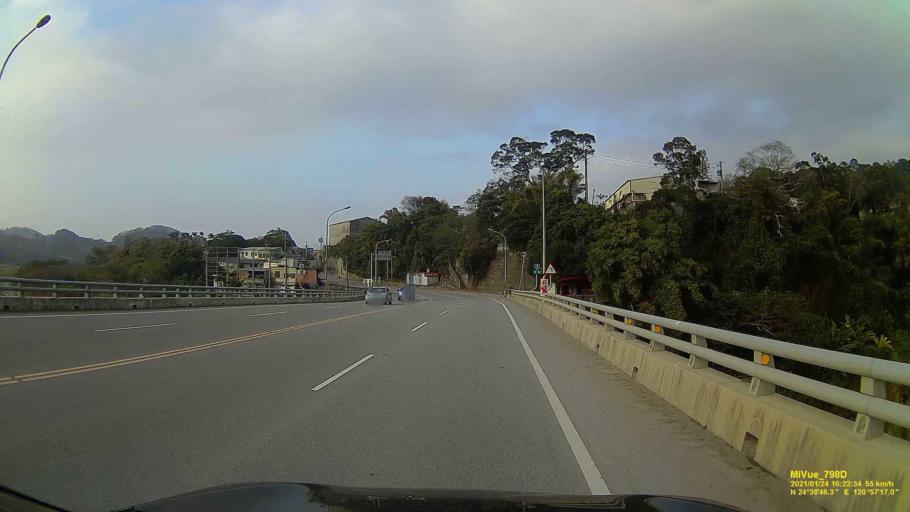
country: TW
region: Taiwan
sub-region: Miaoli
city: Miaoli
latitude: 24.6465
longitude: 120.9548
